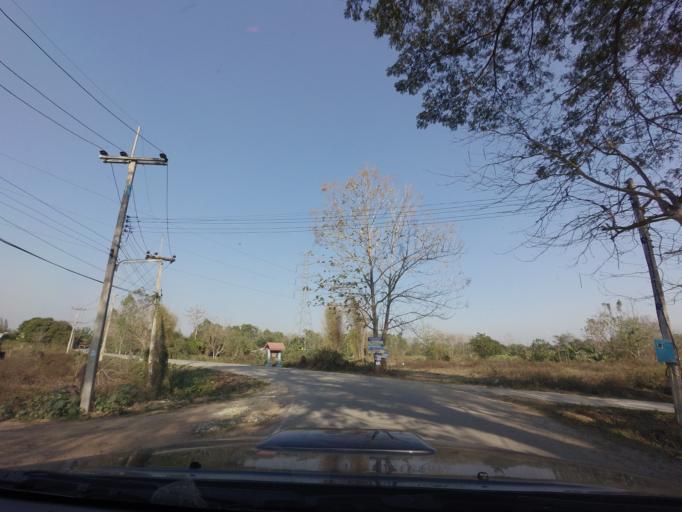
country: TH
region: Chiang Mai
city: San Sai
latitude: 18.9322
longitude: 98.9688
